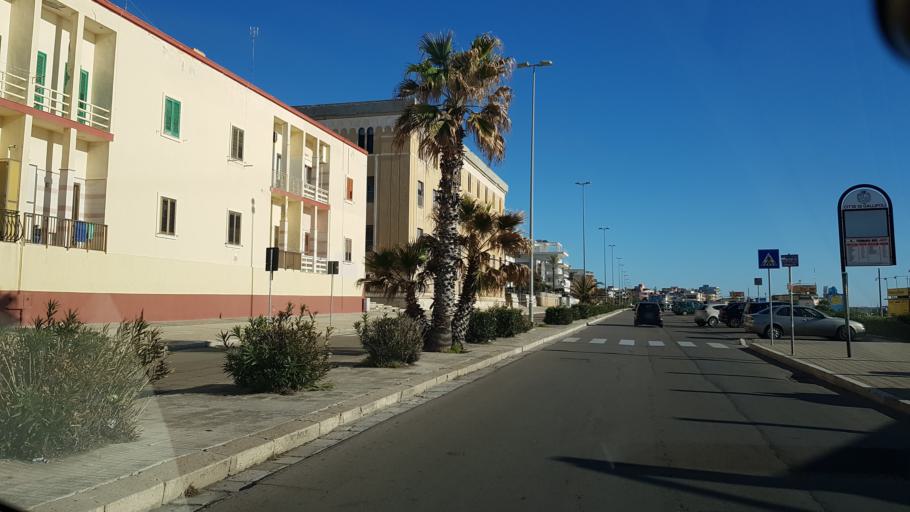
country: IT
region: Apulia
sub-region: Provincia di Lecce
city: Gallipoli
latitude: 40.0528
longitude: 17.9929
